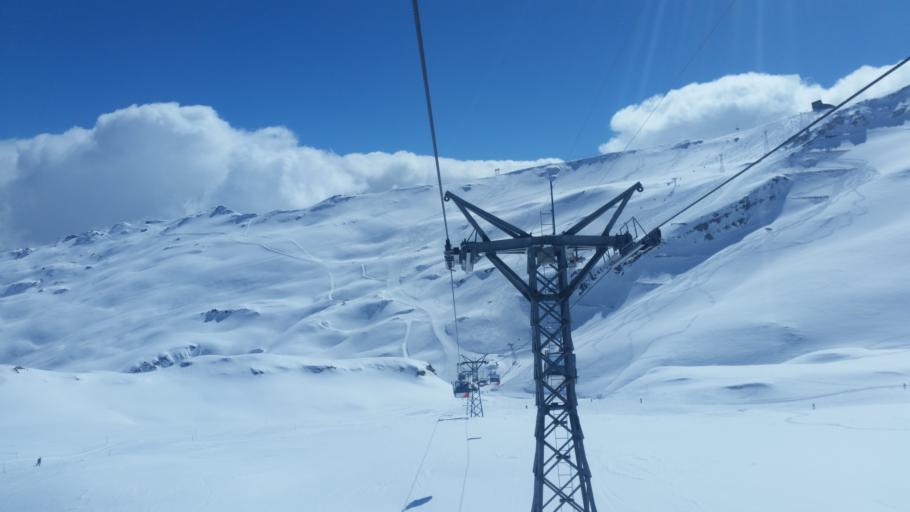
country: CH
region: Grisons
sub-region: Surselva District
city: Ilanz
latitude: 46.8571
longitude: 9.1861
